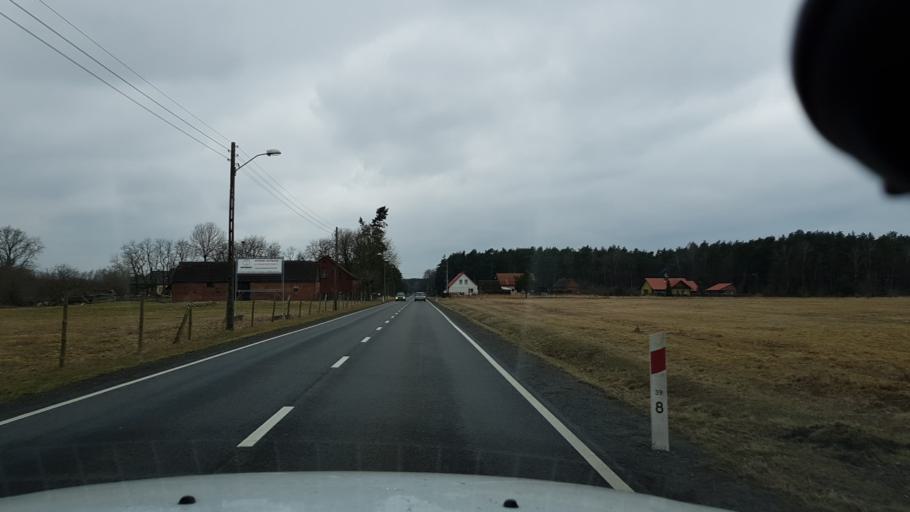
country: PL
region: West Pomeranian Voivodeship
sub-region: Powiat goleniowski
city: Goleniow
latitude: 53.5770
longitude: 14.7544
